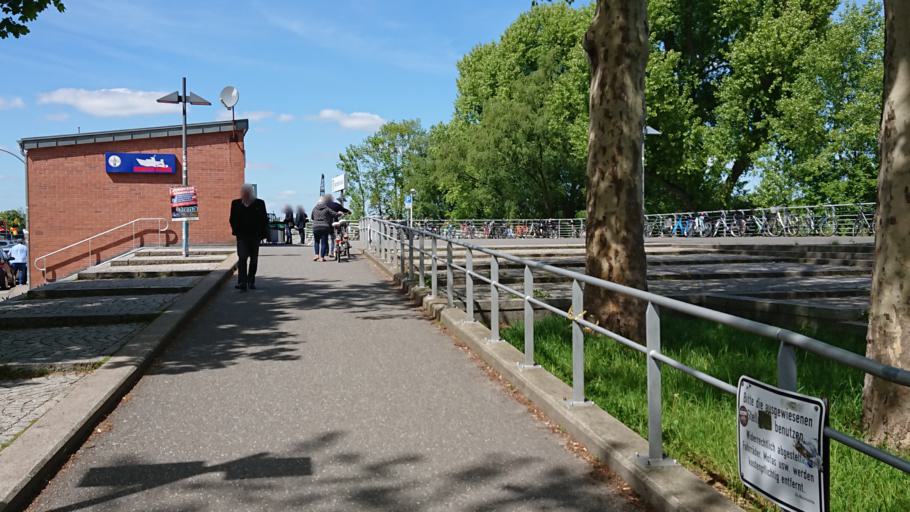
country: DE
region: Hamburg
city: Altona
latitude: 53.5356
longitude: 9.8787
